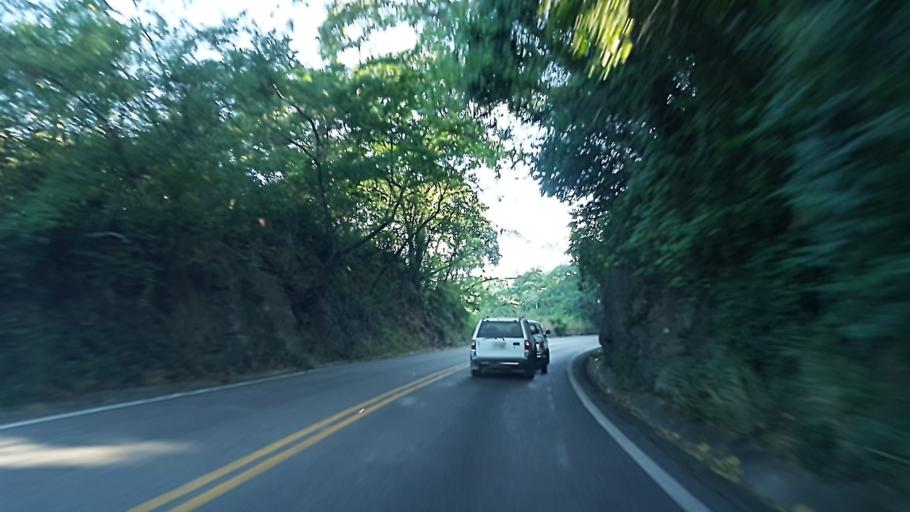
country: MX
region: Nayarit
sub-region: Bahia de Banderas
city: Lo de Marcos
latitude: 20.8798
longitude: -105.4256
